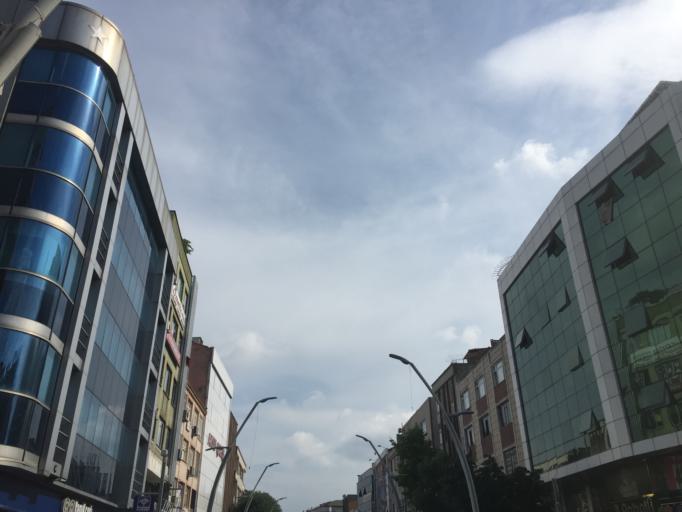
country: TR
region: Istanbul
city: Zeytinburnu
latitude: 40.9914
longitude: 28.9038
